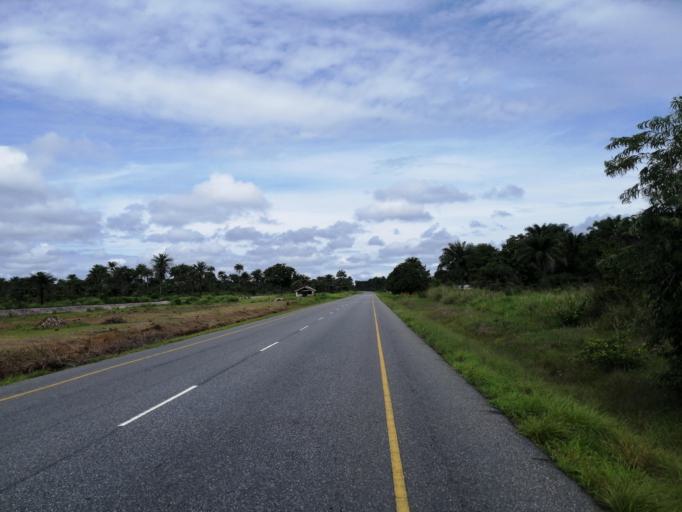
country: SL
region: Northern Province
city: Pepel
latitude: 8.7245
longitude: -12.9552
